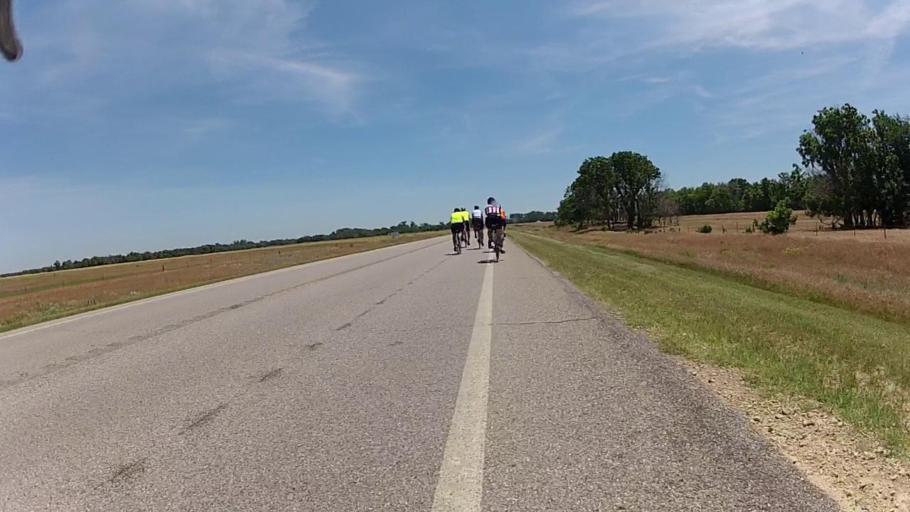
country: US
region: Kansas
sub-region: Barber County
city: Medicine Lodge
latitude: 37.2534
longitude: -98.4658
